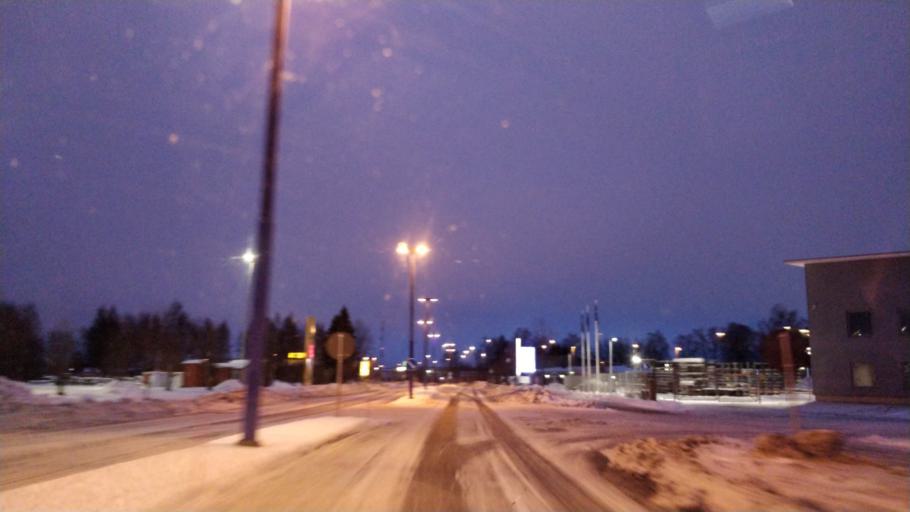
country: FI
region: Lapland
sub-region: Kemi-Tornio
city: Kemi
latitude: 65.7423
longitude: 24.5767
